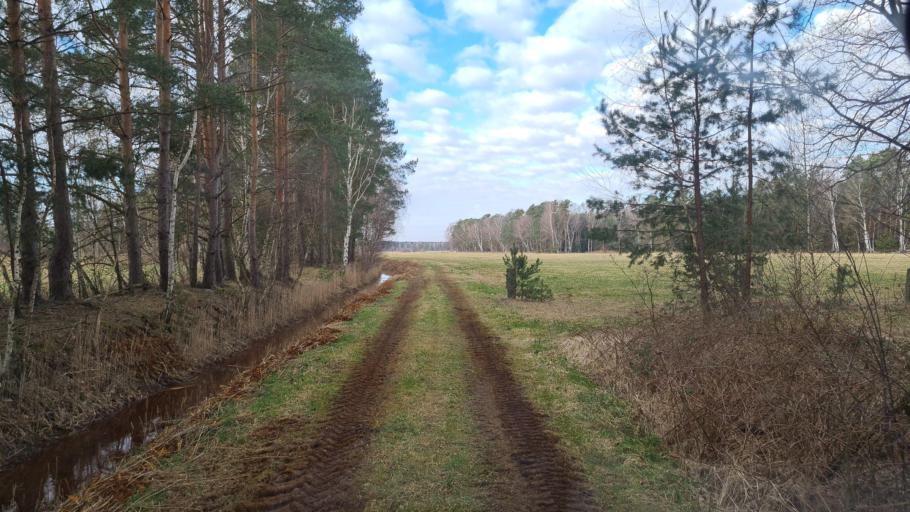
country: DE
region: Brandenburg
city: Finsterwalde
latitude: 51.5545
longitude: 13.6567
